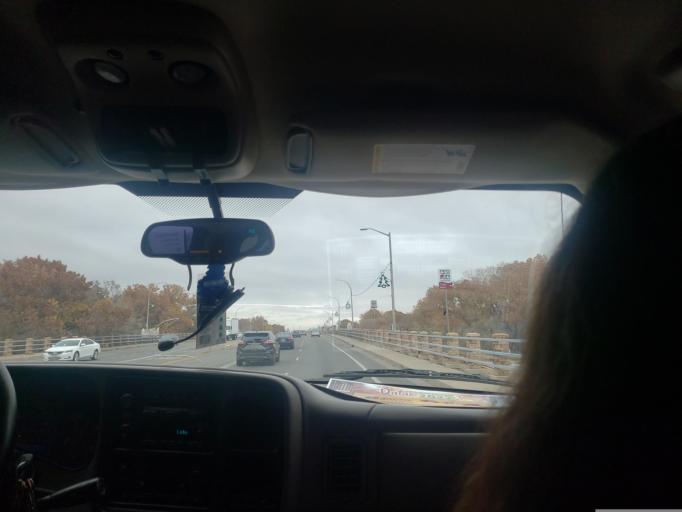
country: US
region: New Mexico
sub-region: Bernalillo County
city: Albuquerque
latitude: 35.0882
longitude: -106.6822
